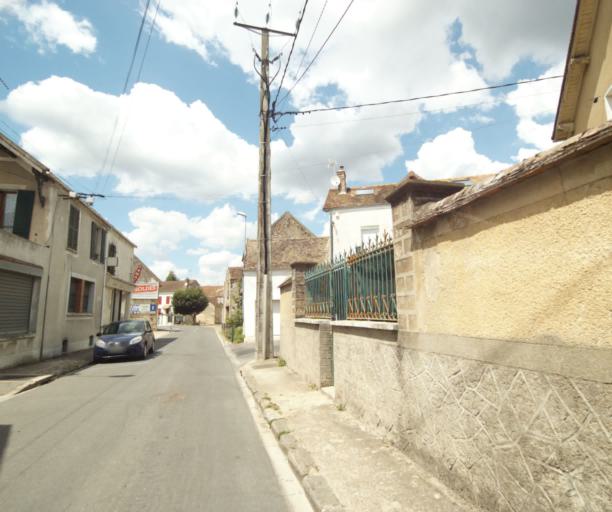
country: FR
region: Ile-de-France
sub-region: Departement de Seine-et-Marne
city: Hericy
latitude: 48.4465
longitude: 2.7752
